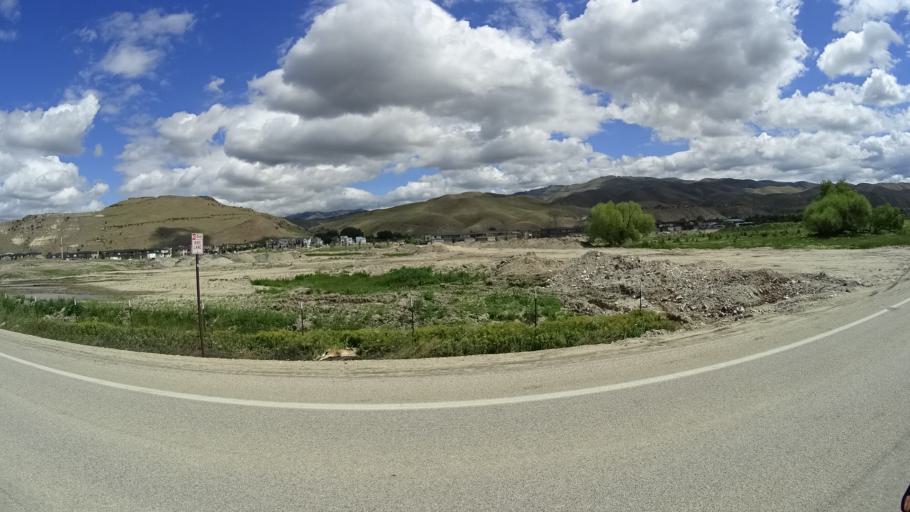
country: US
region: Idaho
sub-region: Ada County
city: Boise
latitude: 43.5707
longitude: -116.1340
